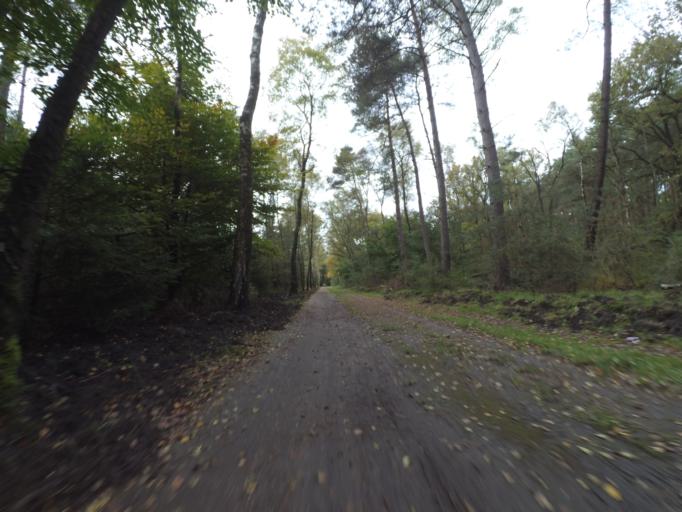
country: NL
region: Gelderland
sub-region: Gemeente Ermelo
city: Ermelo
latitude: 52.3132
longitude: 5.6933
